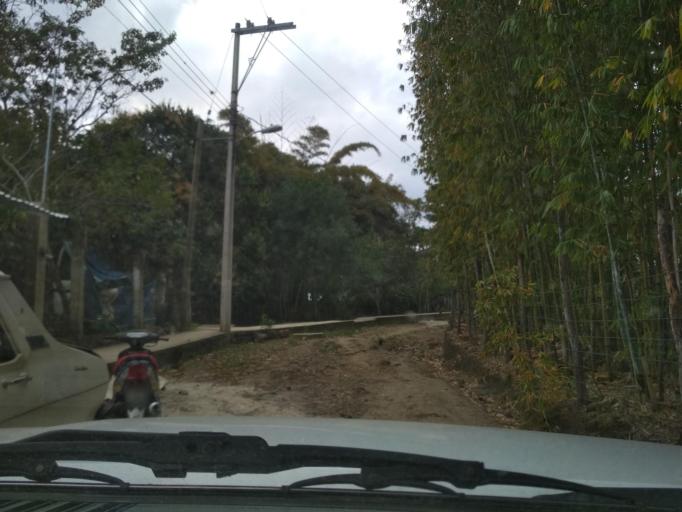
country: MX
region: Veracruz
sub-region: Coatepec
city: Tuzamapan
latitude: 19.3679
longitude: -96.8811
